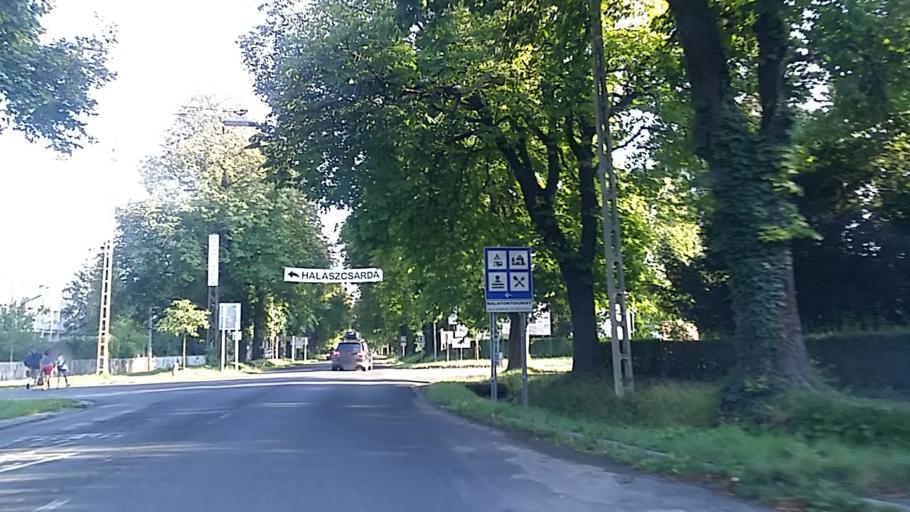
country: HU
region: Zala
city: Keszthely
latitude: 46.7505
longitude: 17.2410
